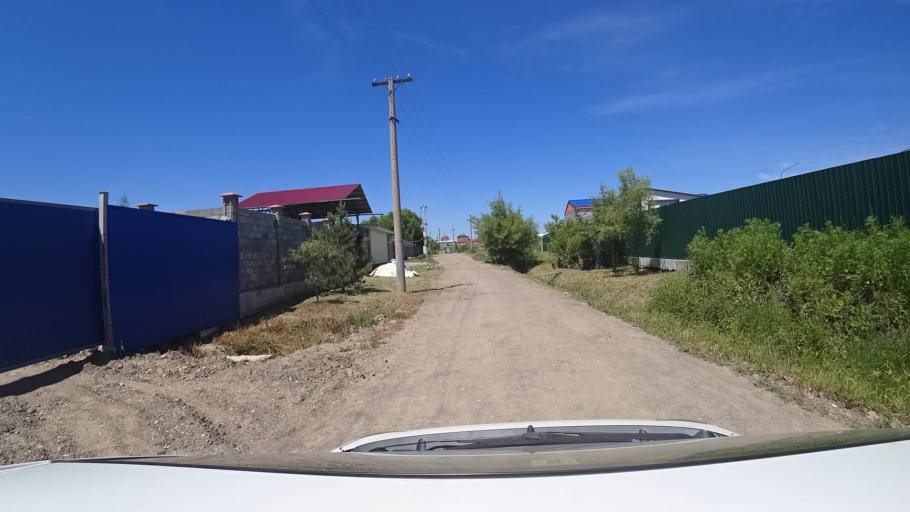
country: RU
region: Khabarovsk Krai
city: Topolevo
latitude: 48.5005
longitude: 135.1822
